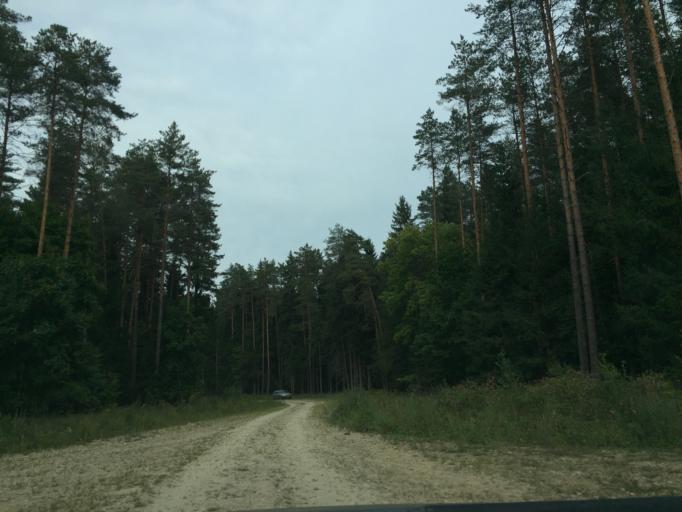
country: LV
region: Baldone
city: Baldone
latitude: 56.7498
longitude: 24.4661
